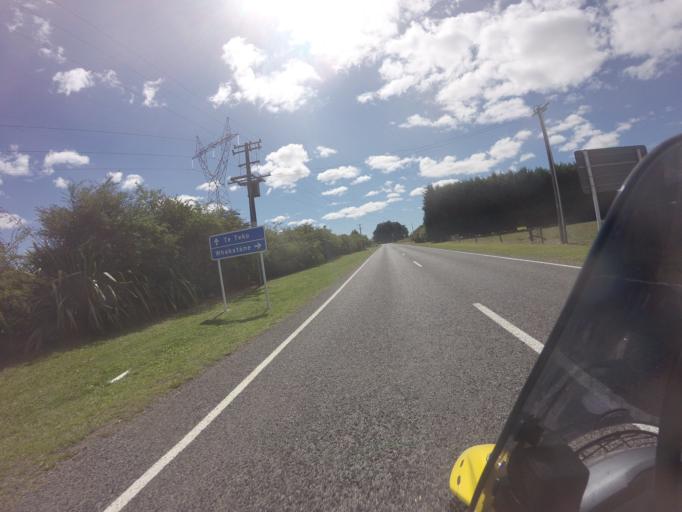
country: NZ
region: Bay of Plenty
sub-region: Whakatane District
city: Edgecumbe
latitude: -38.0731
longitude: 176.8179
